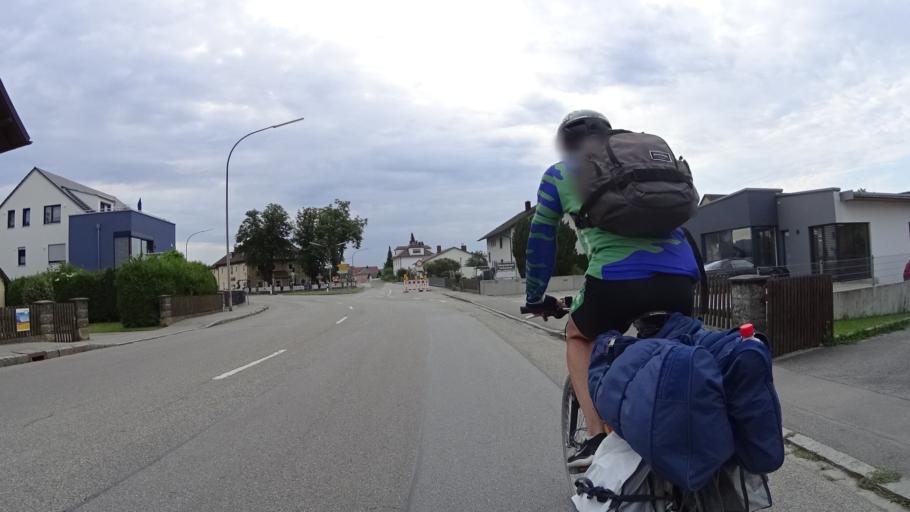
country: DE
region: Bavaria
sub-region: Lower Bavaria
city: Parkstetten
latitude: 48.9164
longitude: 12.6020
